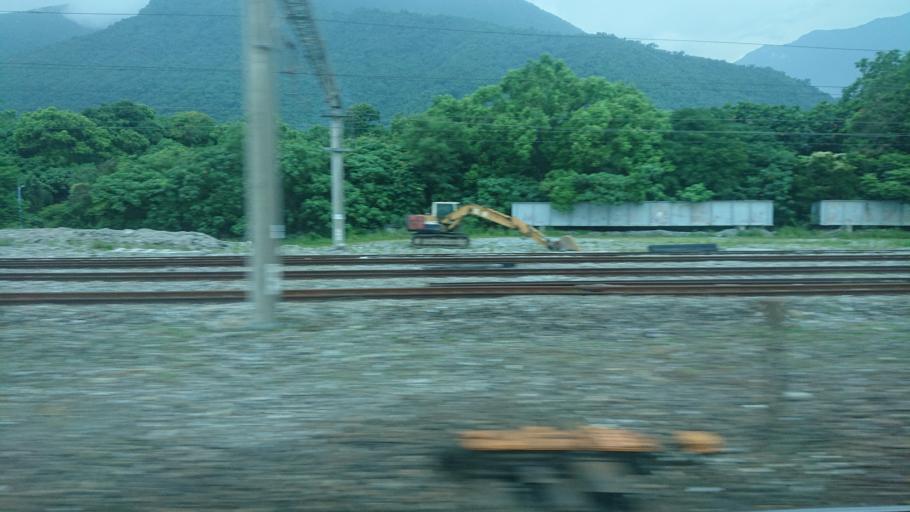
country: TW
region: Taiwan
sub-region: Hualien
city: Hualian
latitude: 24.1260
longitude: 121.6394
